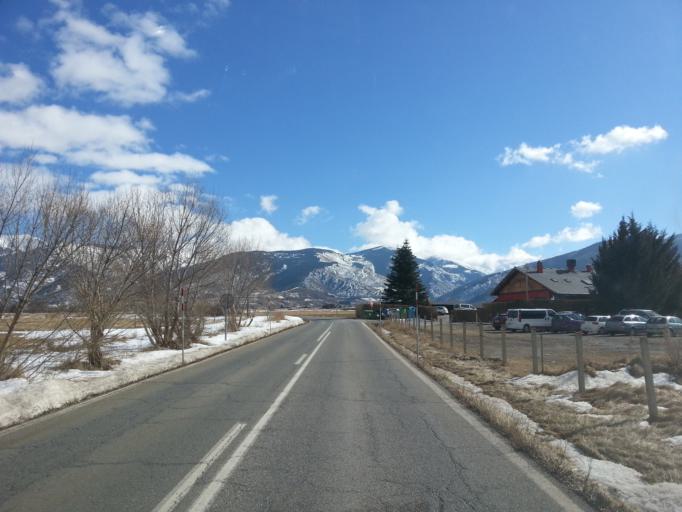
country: ES
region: Catalonia
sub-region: Provincia de Girona
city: Llivia
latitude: 42.4570
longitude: 2.0053
